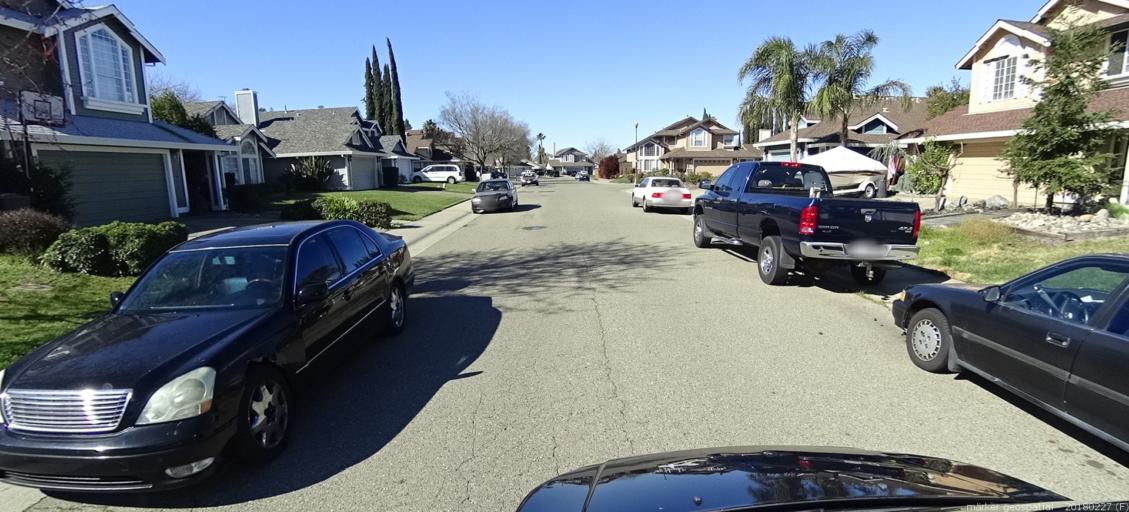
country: US
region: California
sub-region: Sacramento County
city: Antelope
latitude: 38.7219
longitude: -121.3481
